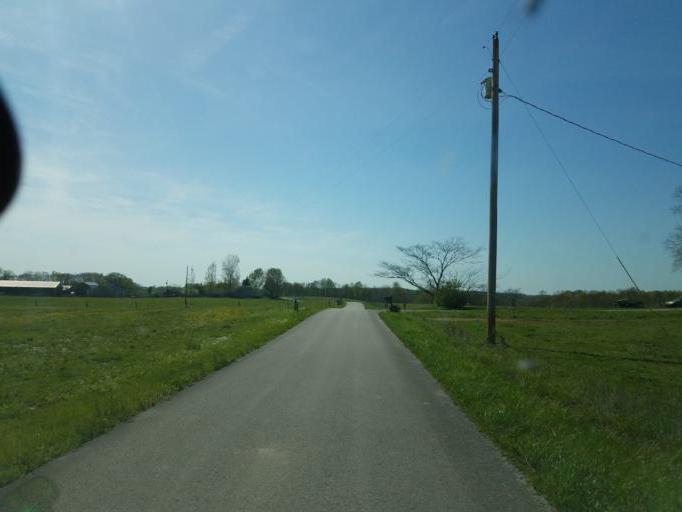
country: US
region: Kentucky
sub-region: Barren County
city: Cave City
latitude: 37.1211
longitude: -86.1189
